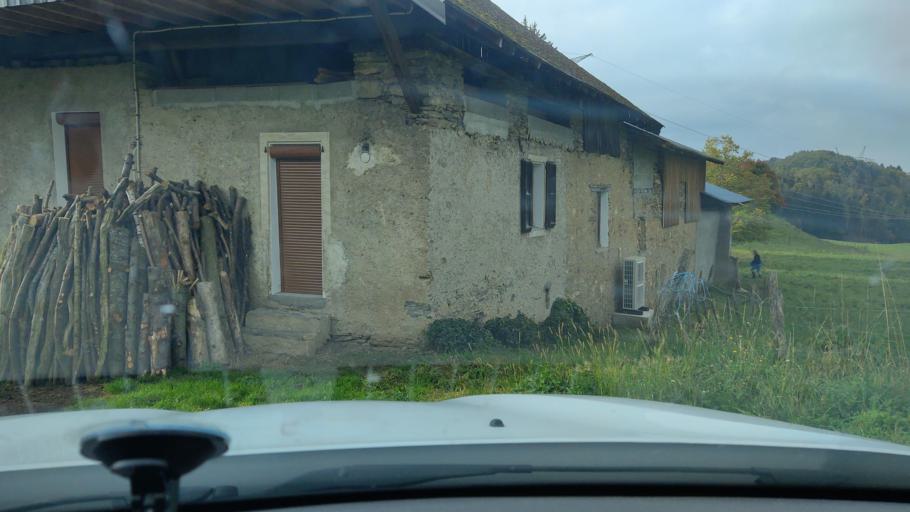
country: FR
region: Rhone-Alpes
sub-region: Departement de la Savoie
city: La Rochette
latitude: 45.4777
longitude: 6.1076
